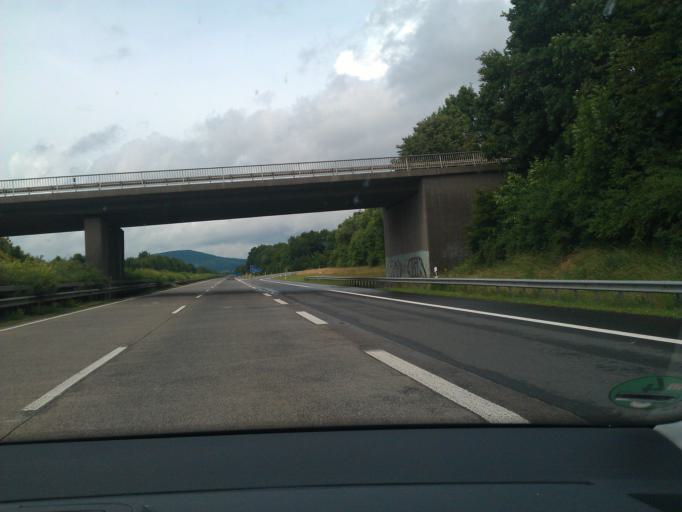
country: DE
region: Rheinland-Pfalz
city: Esch
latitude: 49.9004
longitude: 6.8531
